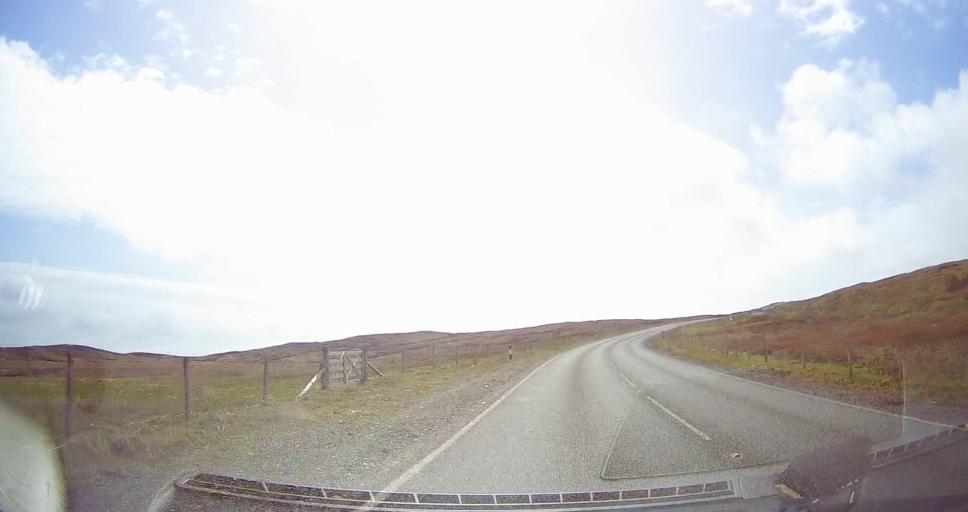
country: GB
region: Scotland
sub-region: Shetland Islands
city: Sandwick
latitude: 60.0929
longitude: -1.2291
